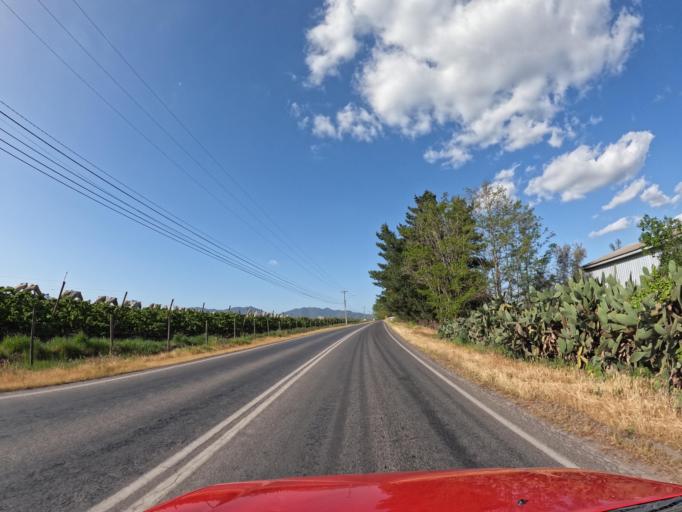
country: CL
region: Maule
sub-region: Provincia de Curico
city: Rauco
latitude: -34.9018
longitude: -71.2761
